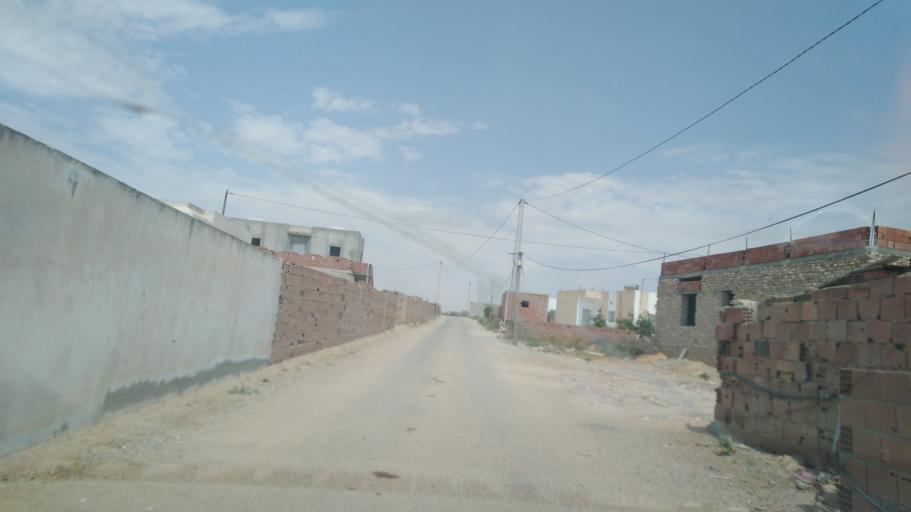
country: TN
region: Safaqis
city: Sfax
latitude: 34.7436
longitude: 10.5605
